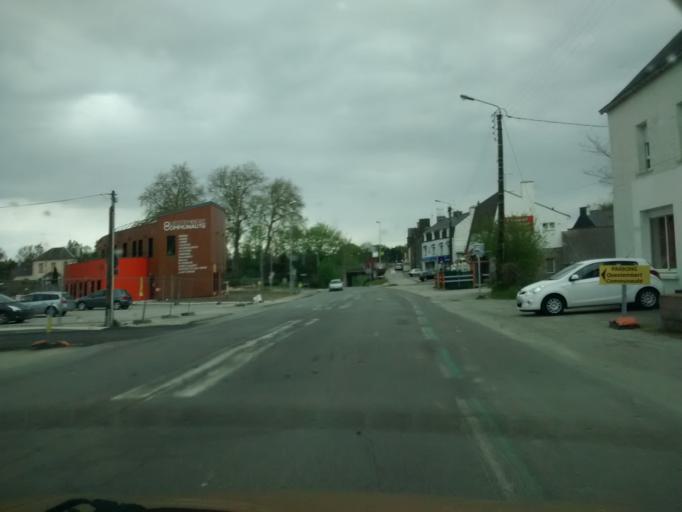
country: FR
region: Brittany
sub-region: Departement du Morbihan
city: Questembert
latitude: 47.6814
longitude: -2.4491
